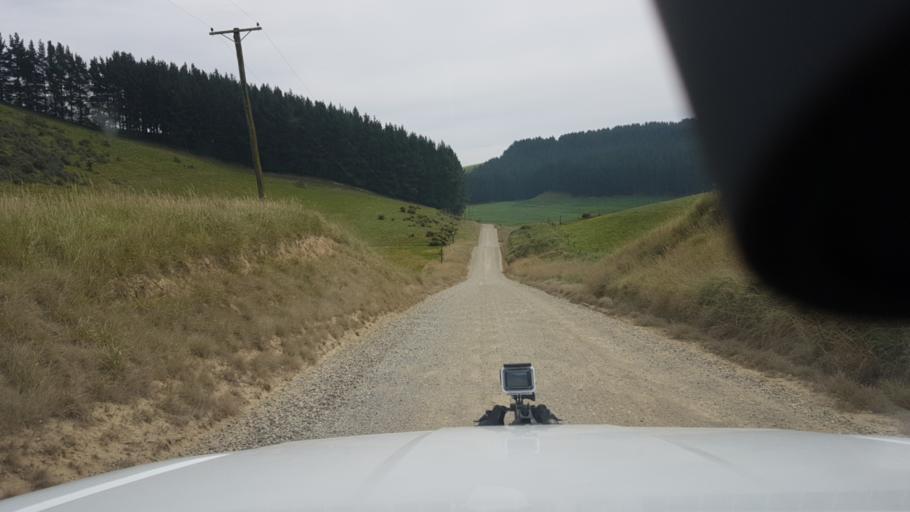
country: NZ
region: Otago
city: Oamaru
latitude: -45.0183
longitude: 170.9114
